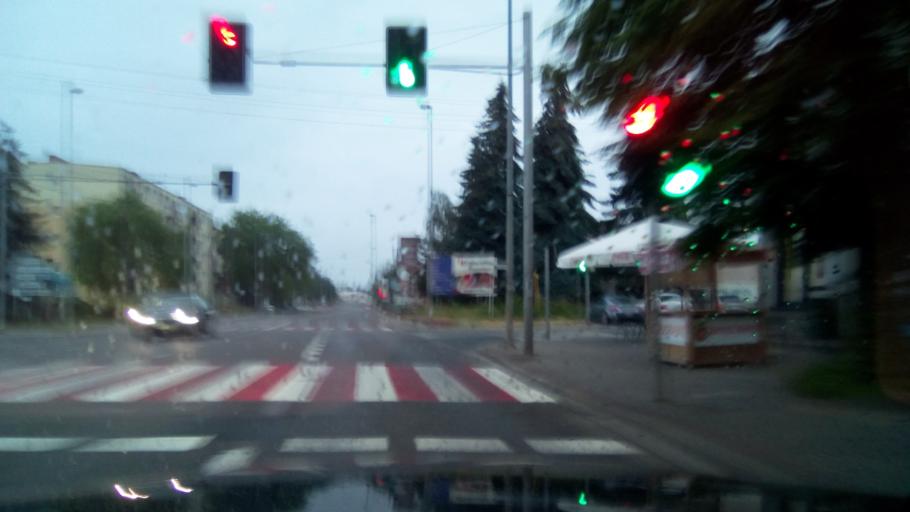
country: PL
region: Greater Poland Voivodeship
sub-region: Powiat poznanski
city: Swarzedz
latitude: 52.4125
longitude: 17.0852
